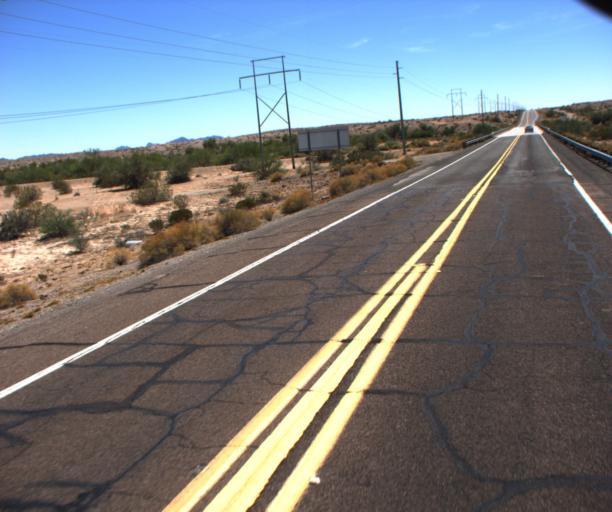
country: US
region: Arizona
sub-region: La Paz County
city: Parker
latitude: 33.9923
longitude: -114.2169
